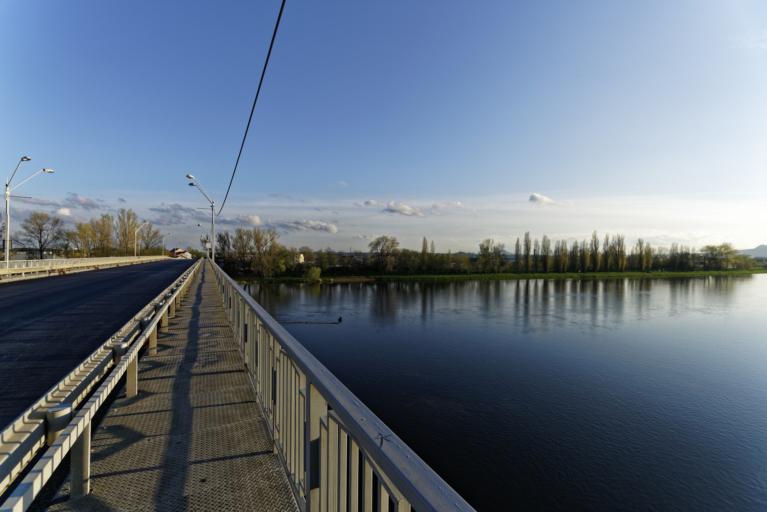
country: CZ
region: Ustecky
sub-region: Okres Litomerice
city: Litomerice
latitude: 50.5302
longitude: 14.1346
